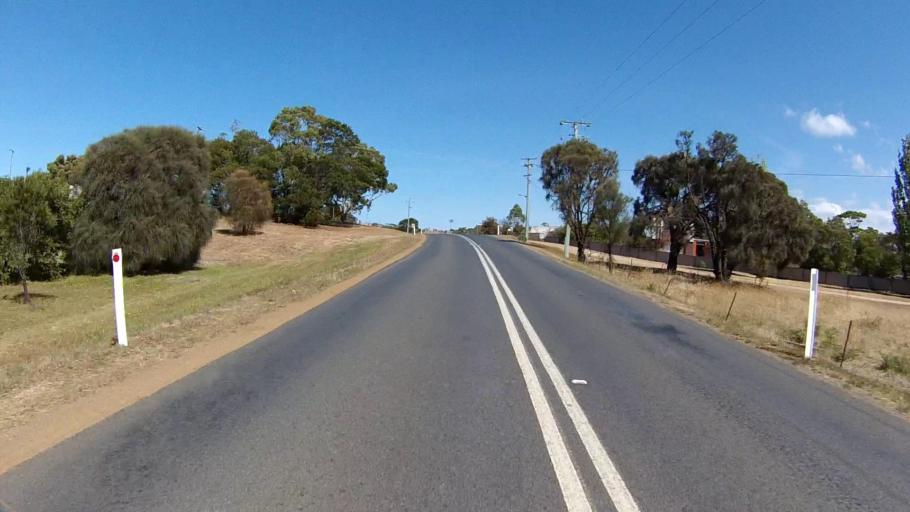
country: AU
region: Tasmania
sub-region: Sorell
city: Sorell
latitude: -42.1330
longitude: 148.0715
